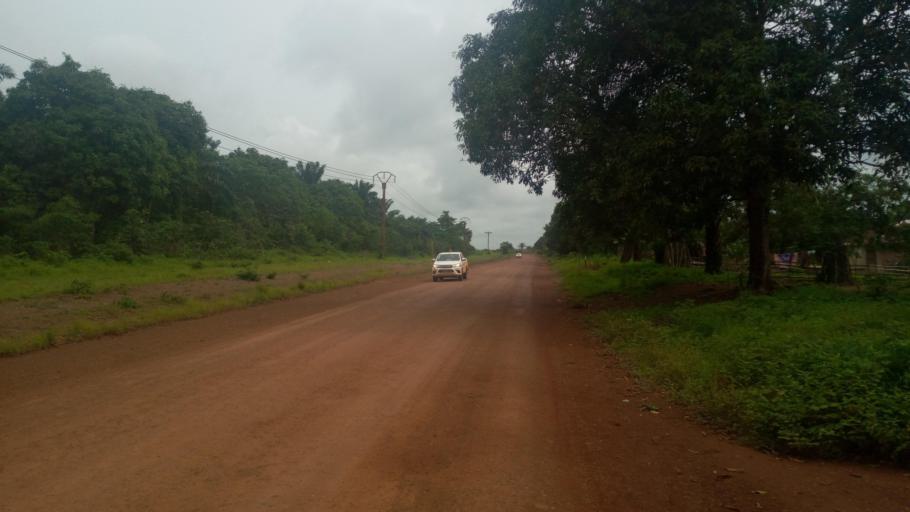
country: SL
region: Southern Province
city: Mogbwemo
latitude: 7.7332
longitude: -12.2784
